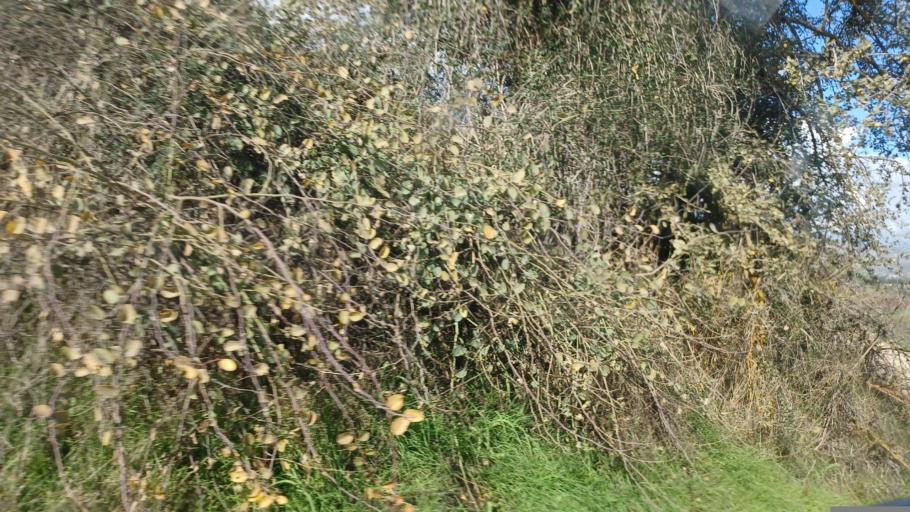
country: CY
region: Pafos
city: Mesogi
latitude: 34.8349
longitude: 32.5508
